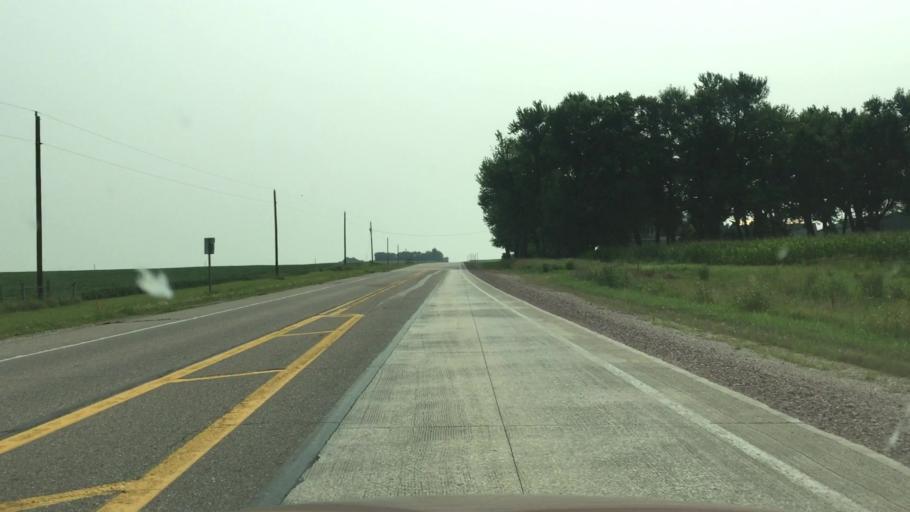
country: US
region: Iowa
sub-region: Osceola County
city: Sibley
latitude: 43.4326
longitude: -95.7098
